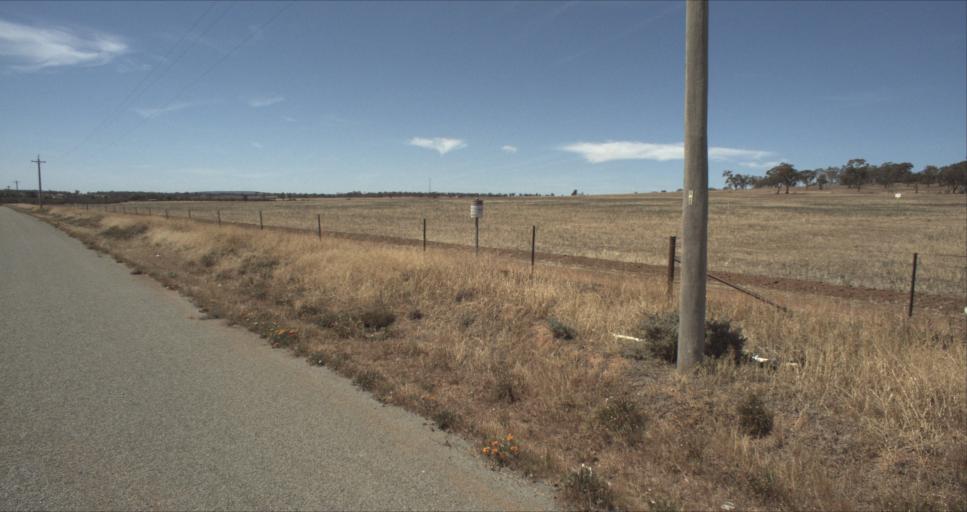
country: AU
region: New South Wales
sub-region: Leeton
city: Leeton
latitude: -34.6102
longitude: 146.4346
